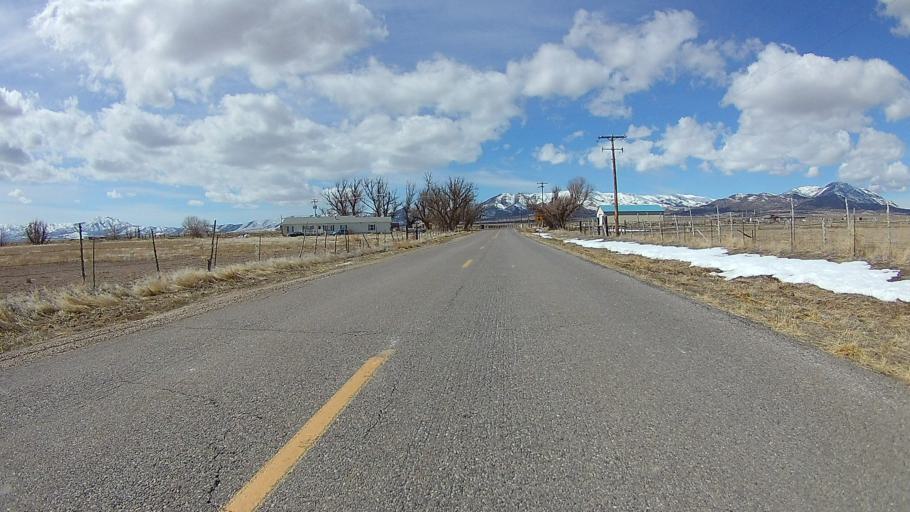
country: US
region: Utah
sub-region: Tooele County
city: Tooele
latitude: 40.1737
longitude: -112.4245
